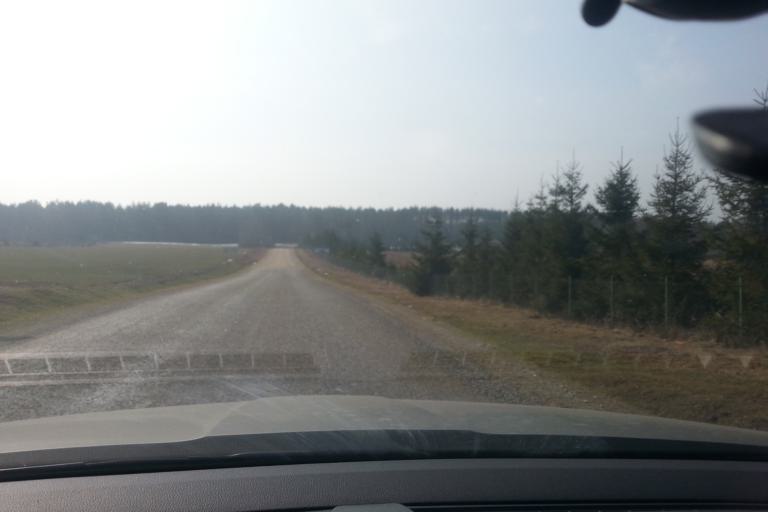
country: LT
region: Vilnius County
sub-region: Trakai
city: Rudiskes
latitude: 54.5157
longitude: 24.9373
